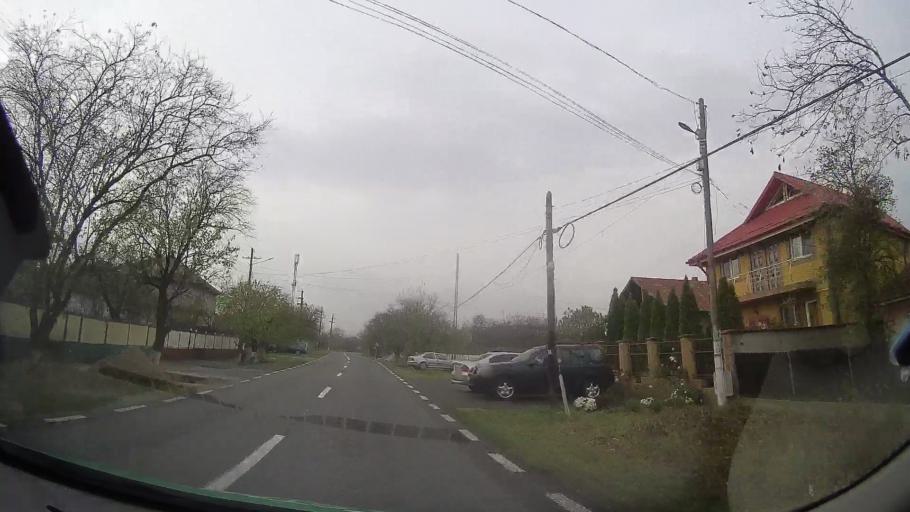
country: RO
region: Ilfov
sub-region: Comuna Gruiu
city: Lipia
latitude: 44.7147
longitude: 26.2548
